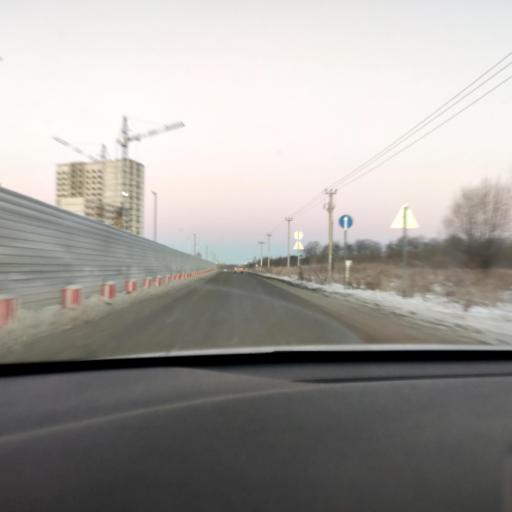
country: RU
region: Tatarstan
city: Osinovo
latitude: 55.8591
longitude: 48.9082
